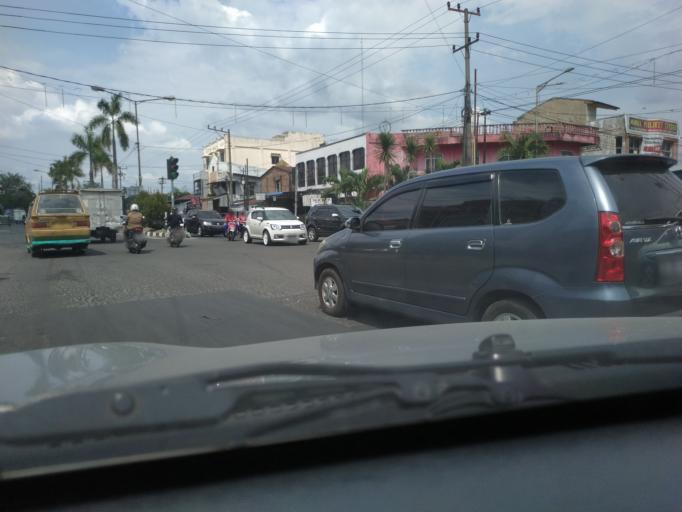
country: ID
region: North Sumatra
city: Medan
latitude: 3.5843
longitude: 98.6411
